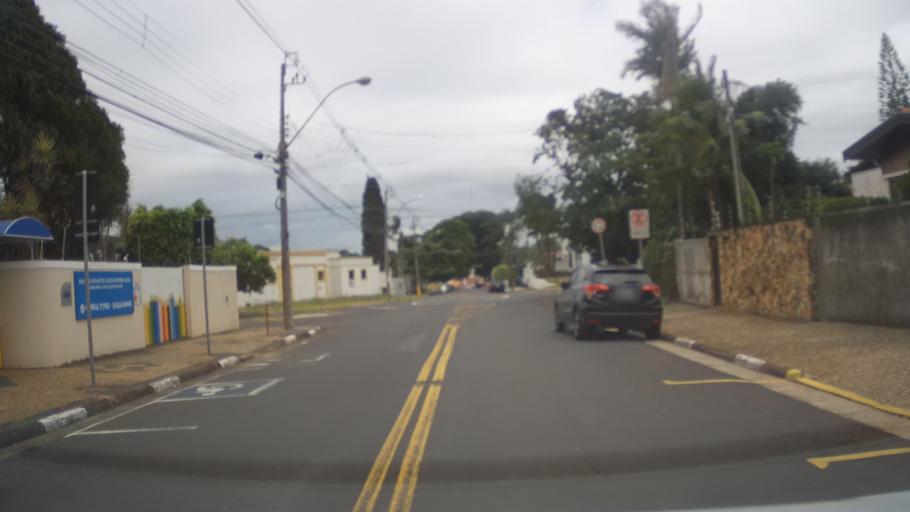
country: BR
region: Sao Paulo
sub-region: Campinas
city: Campinas
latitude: -22.9003
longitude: -47.0409
